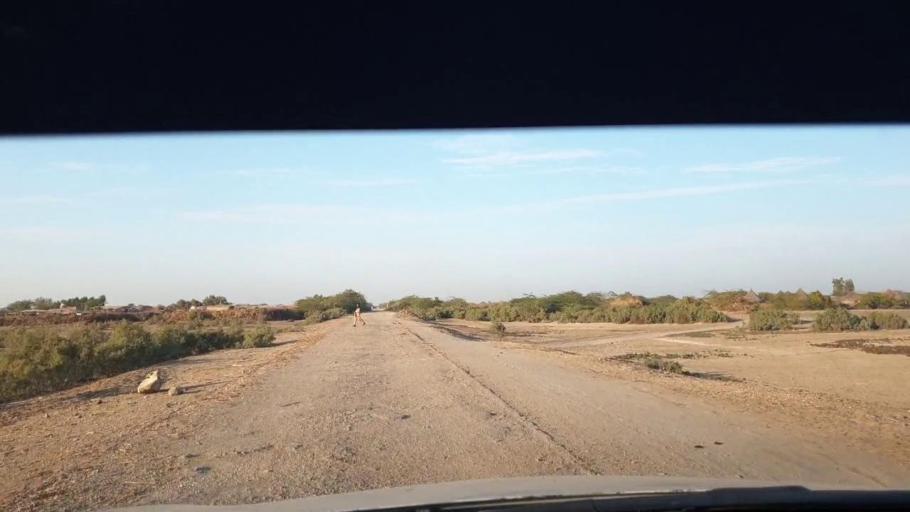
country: PK
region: Sindh
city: Berani
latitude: 25.8022
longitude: 68.8825
